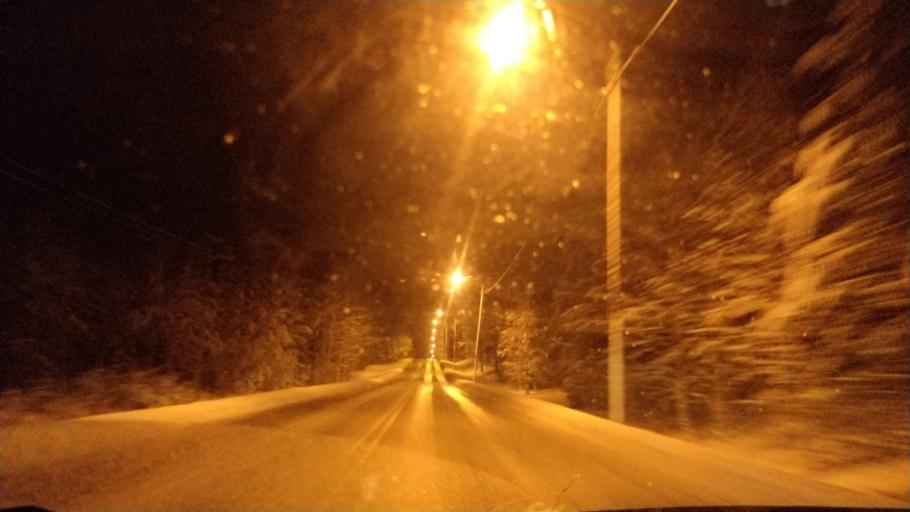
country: FI
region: Lapland
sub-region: Rovaniemi
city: Rovaniemi
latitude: 66.3006
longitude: 25.3536
